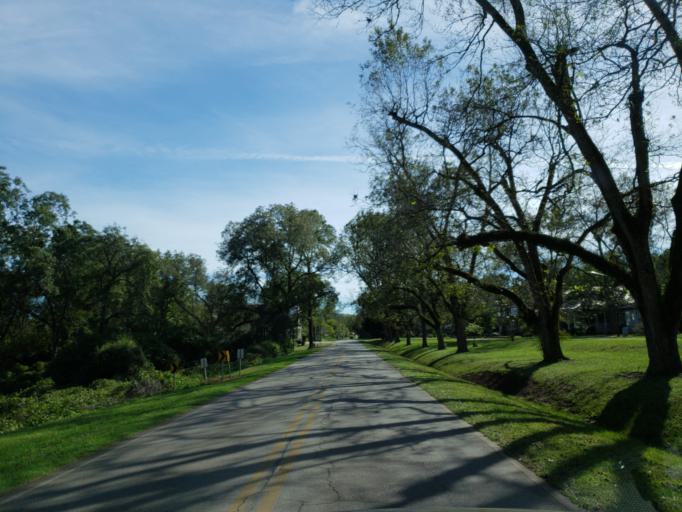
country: US
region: Georgia
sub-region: Crawford County
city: Roberta
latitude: 32.8691
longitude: -84.0924
